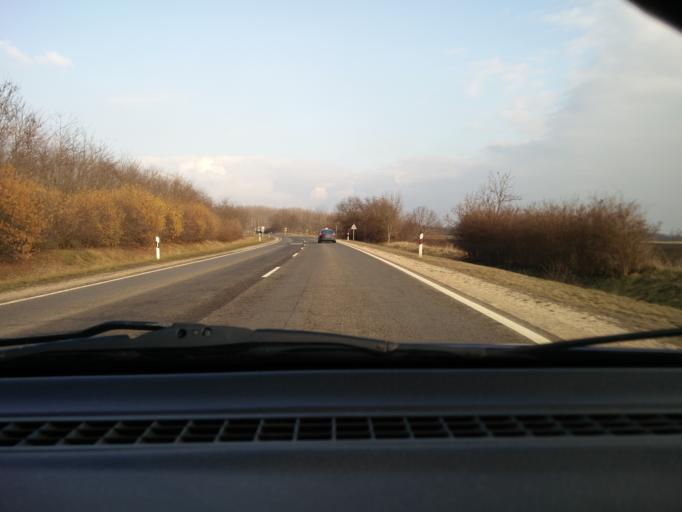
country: HU
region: Pest
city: Nyaregyhaza
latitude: 47.2465
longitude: 19.4906
